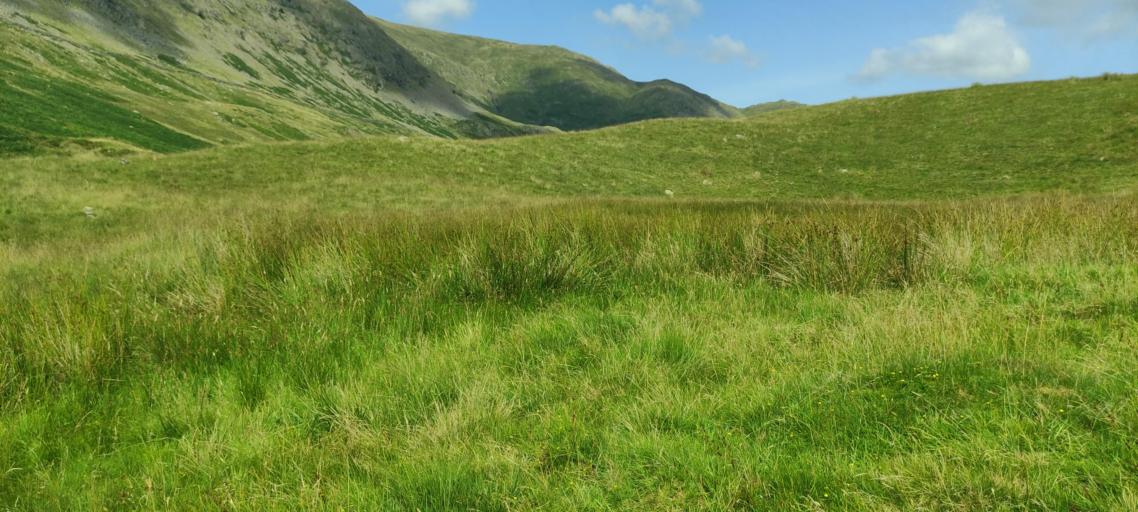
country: GB
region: England
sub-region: Cumbria
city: Ambleside
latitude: 54.4624
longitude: -2.9600
